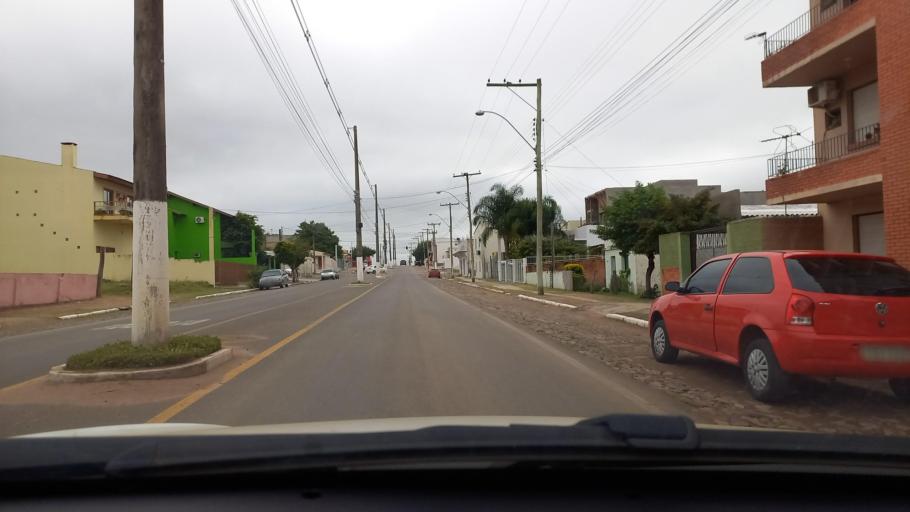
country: BR
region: Rio Grande do Sul
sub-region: Dom Pedrito
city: Dom Pedrito
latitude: -30.9825
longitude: -54.6666
